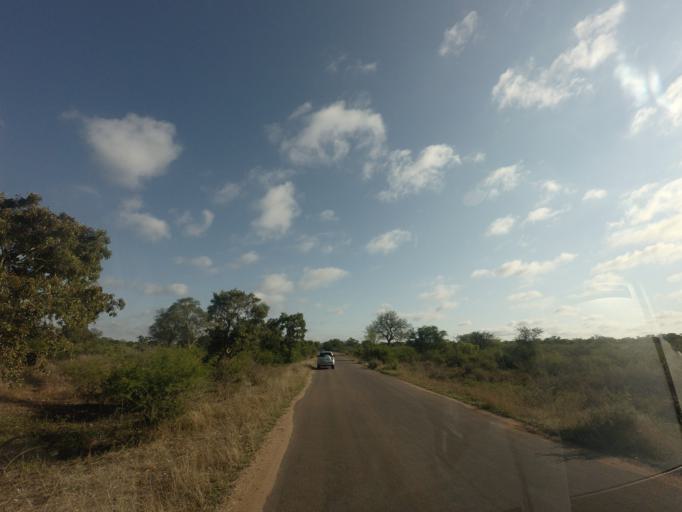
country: ZA
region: Mpumalanga
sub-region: Ehlanzeni District
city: Komatipoort
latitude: -25.2607
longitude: 31.8464
